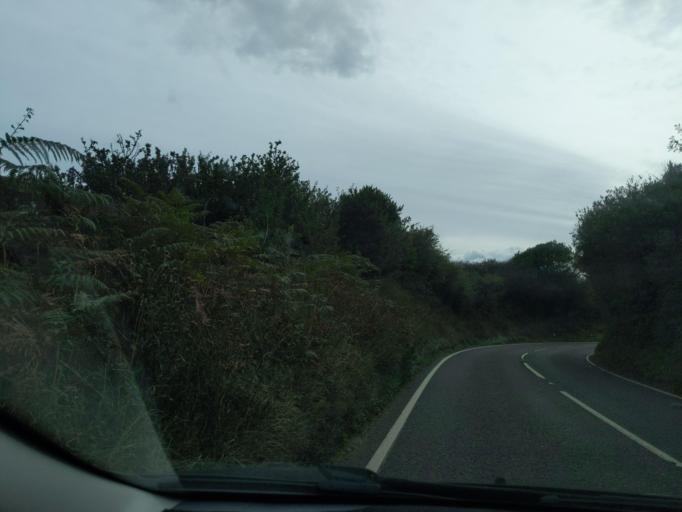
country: GB
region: England
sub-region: Cornwall
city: Mevagissey
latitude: 50.2879
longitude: -4.7863
